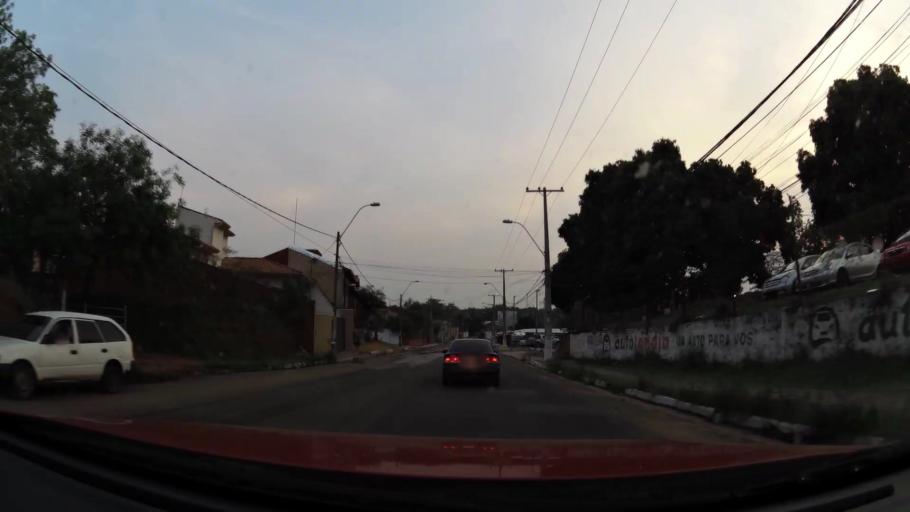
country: PY
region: Central
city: Lambare
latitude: -25.3393
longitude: -57.6232
